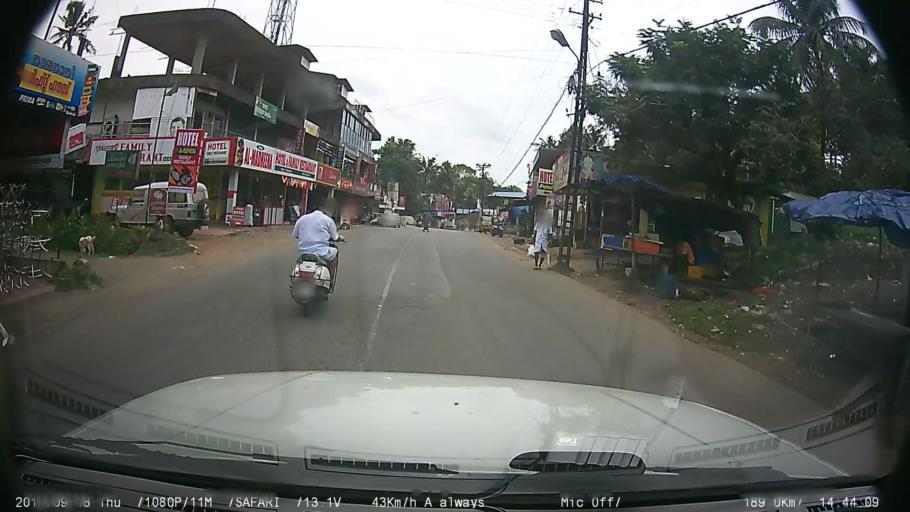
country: IN
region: Kerala
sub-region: Ernakulam
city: Muvattupula
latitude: 9.9970
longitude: 76.5969
